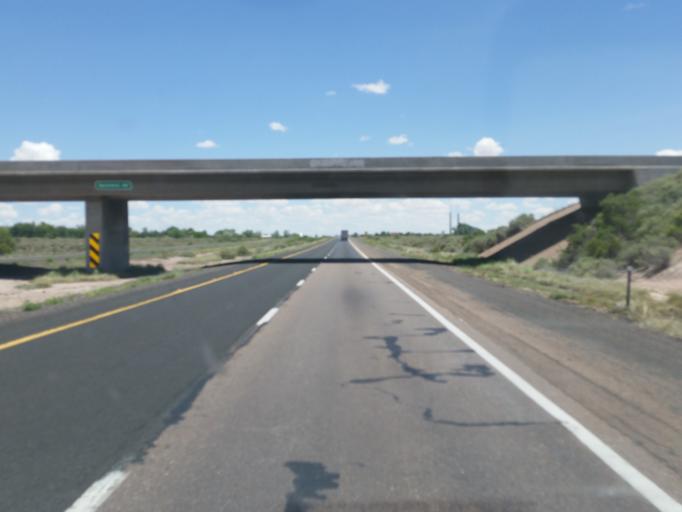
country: US
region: Arizona
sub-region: Navajo County
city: Joseph City
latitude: 34.9562
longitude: -110.3521
